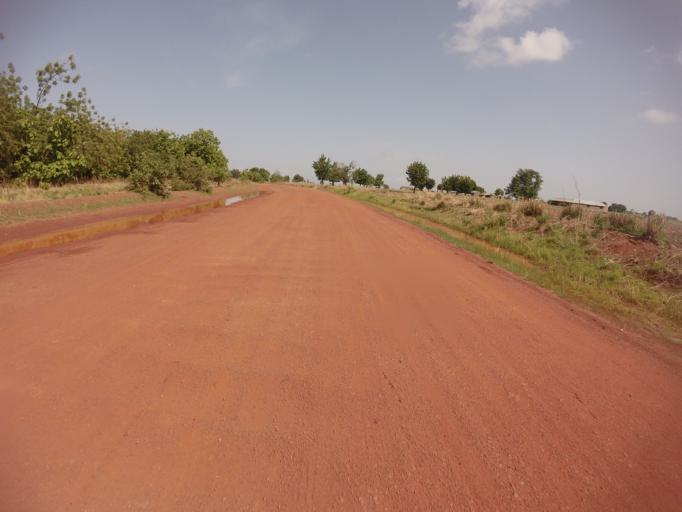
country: GH
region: Upper East
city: Bawku
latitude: 11.0066
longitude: -0.2004
